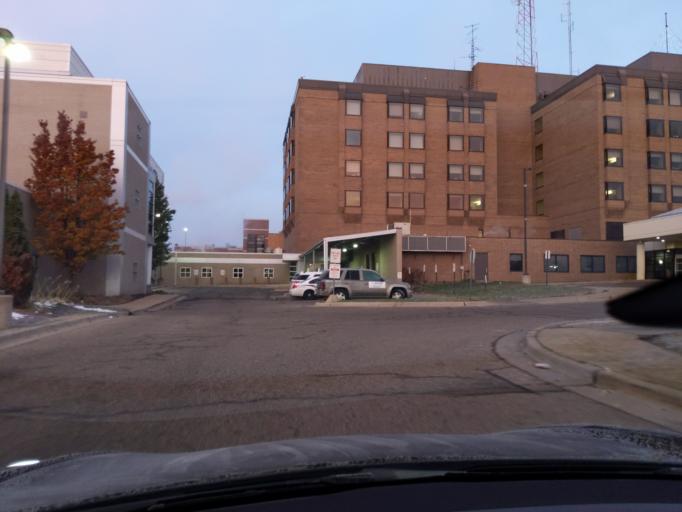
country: US
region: Michigan
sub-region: Ingham County
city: Lansing
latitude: 42.7035
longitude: -84.5542
